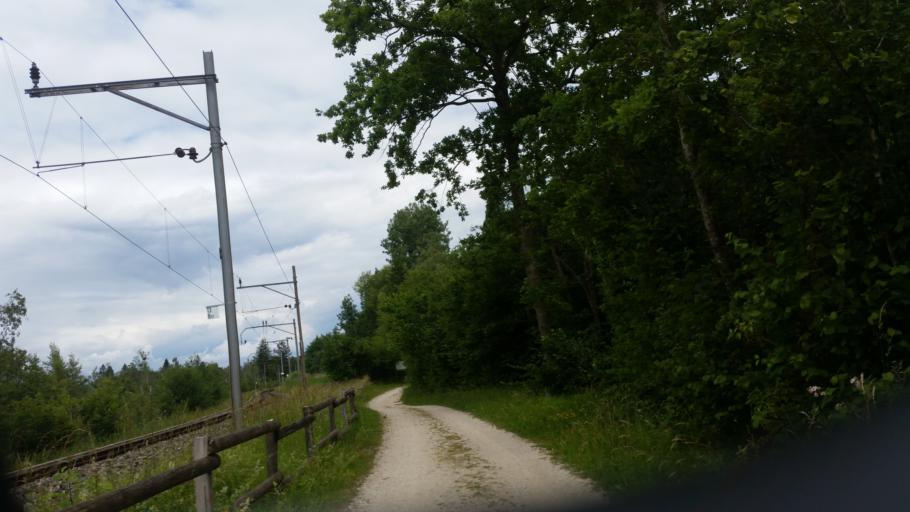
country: CH
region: Fribourg
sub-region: Broye District
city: Estavayer-le-Lac
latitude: 46.8241
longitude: 6.7975
